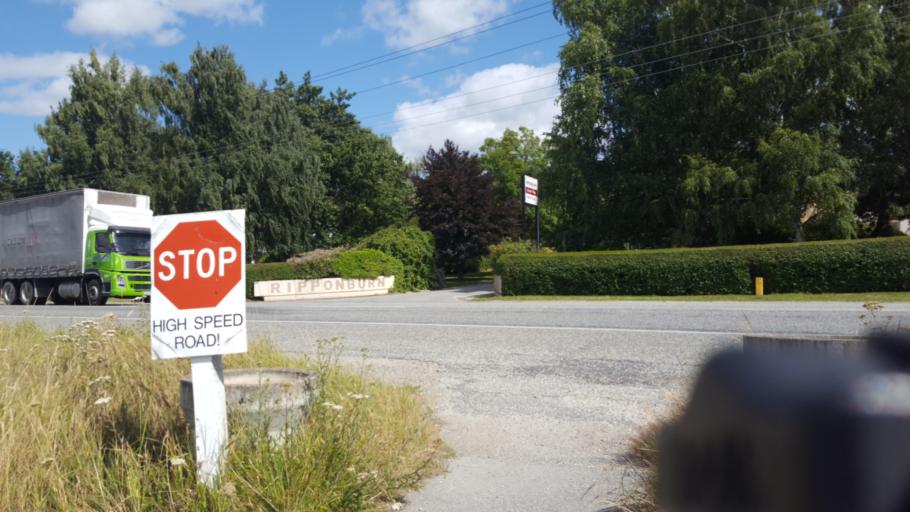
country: NZ
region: Otago
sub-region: Queenstown-Lakes District
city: Wanaka
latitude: -45.0387
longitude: 169.1822
